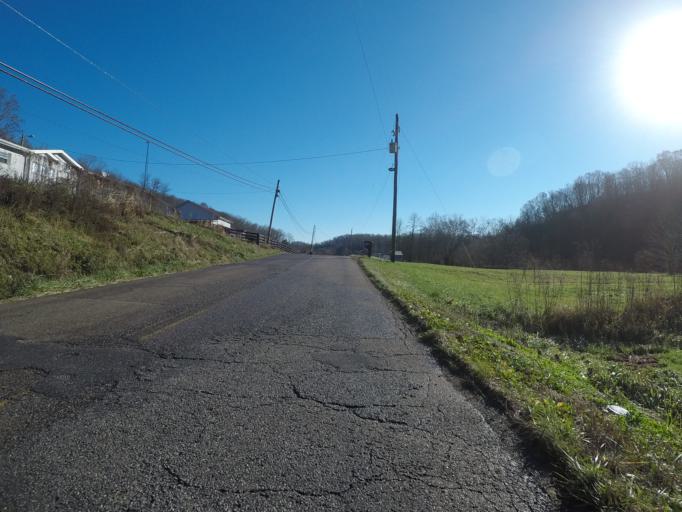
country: US
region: West Virginia
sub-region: Cabell County
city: Huntington
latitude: 38.4818
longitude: -82.4765
